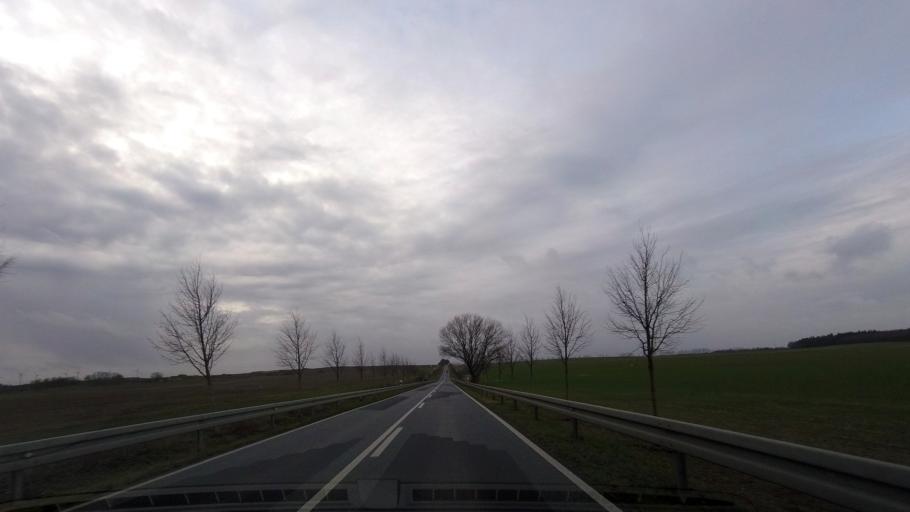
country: DE
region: Mecklenburg-Vorpommern
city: Robel
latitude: 53.3670
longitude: 12.5623
